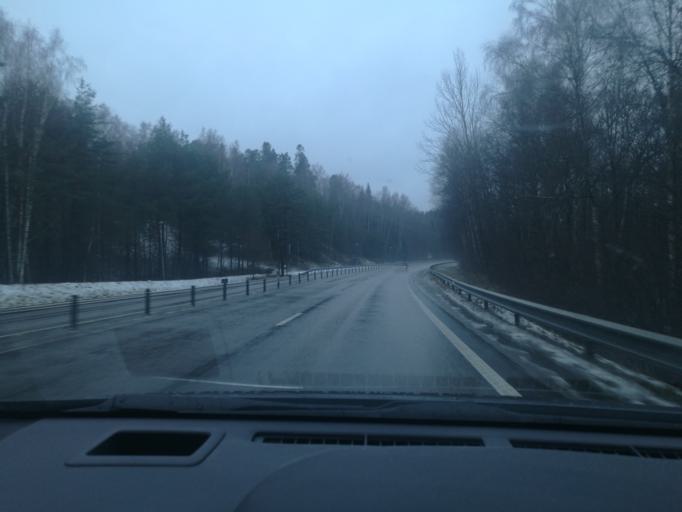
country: SE
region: OEstergoetland
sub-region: Norrkopings Kommun
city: Jursla
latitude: 58.6765
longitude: 16.1504
